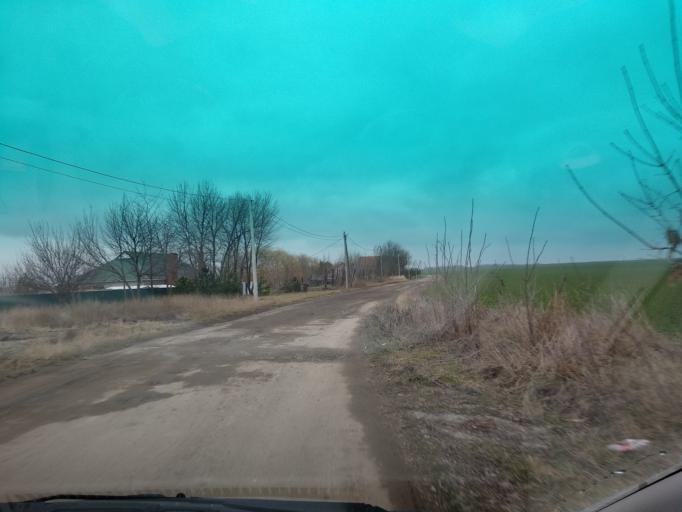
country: RU
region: Krasnodarskiy
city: Vyselki
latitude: 45.6639
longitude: 39.7015
